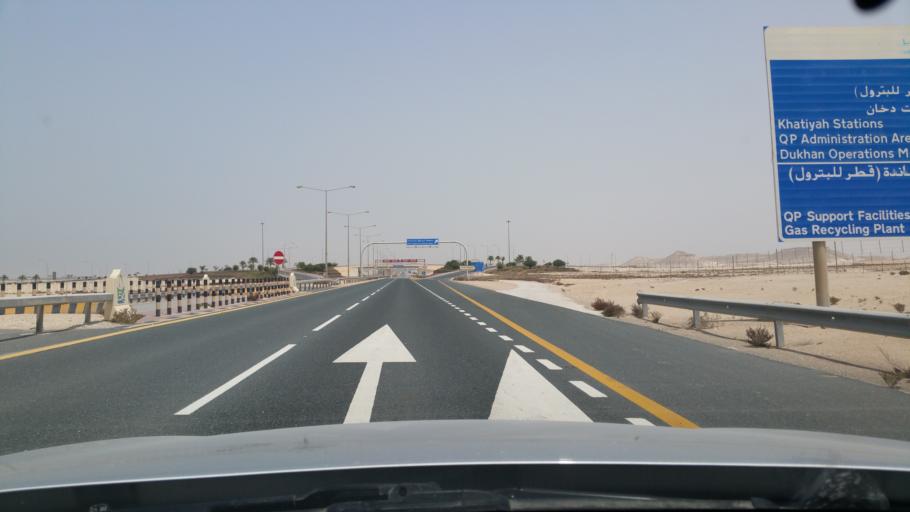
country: QA
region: Baladiyat ar Rayyan
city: Dukhan
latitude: 25.3834
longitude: 50.7821
